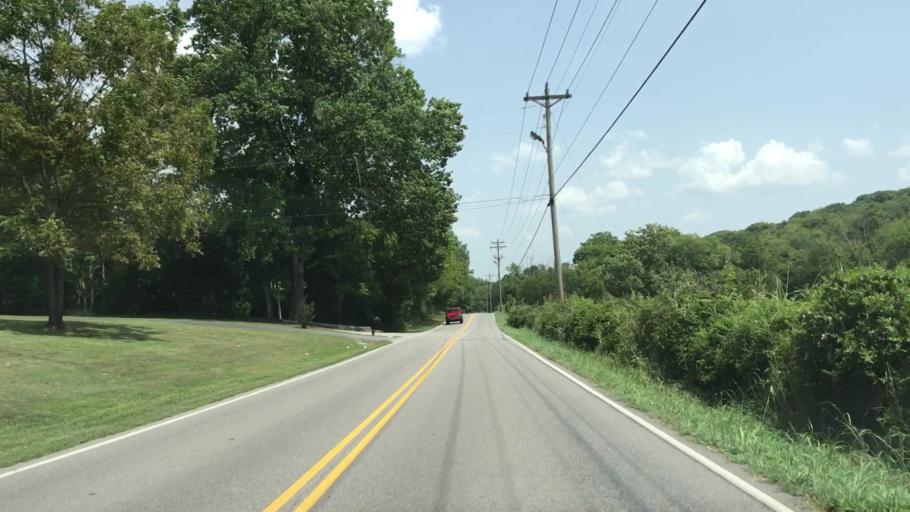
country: US
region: Tennessee
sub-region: Rutherford County
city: La Vergne
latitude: 35.9575
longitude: -86.5923
